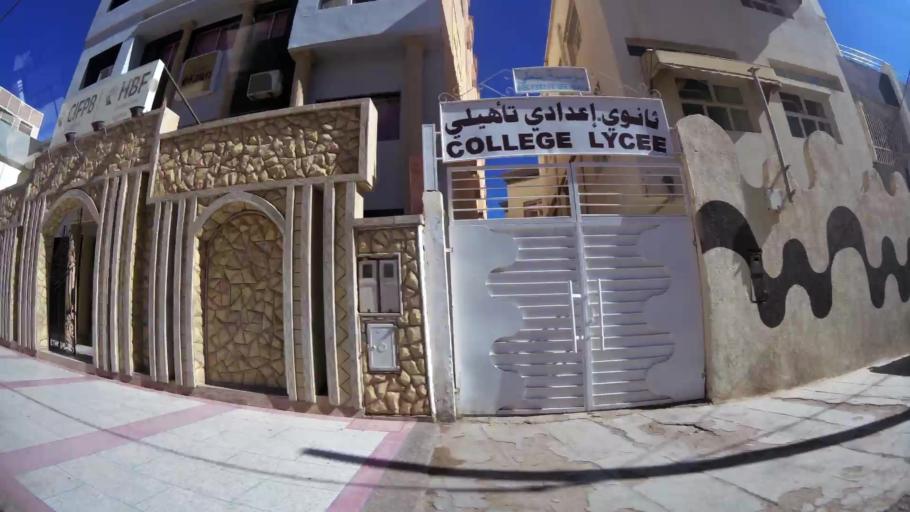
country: MA
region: Oriental
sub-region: Oujda-Angad
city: Oujda
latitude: 34.6593
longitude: -1.8973
